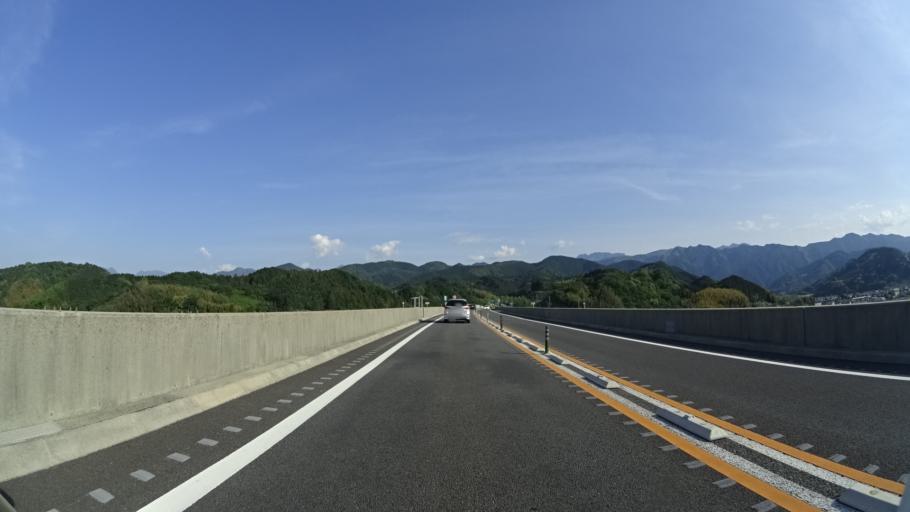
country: JP
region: Ehime
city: Saijo
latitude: 33.8904
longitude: 133.0855
